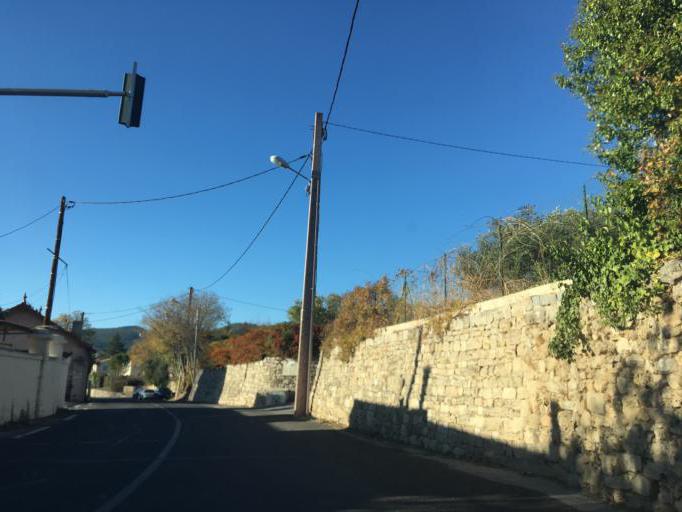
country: FR
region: Provence-Alpes-Cote d'Azur
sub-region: Departement du Var
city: Draguignan
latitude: 43.5449
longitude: 6.4554
